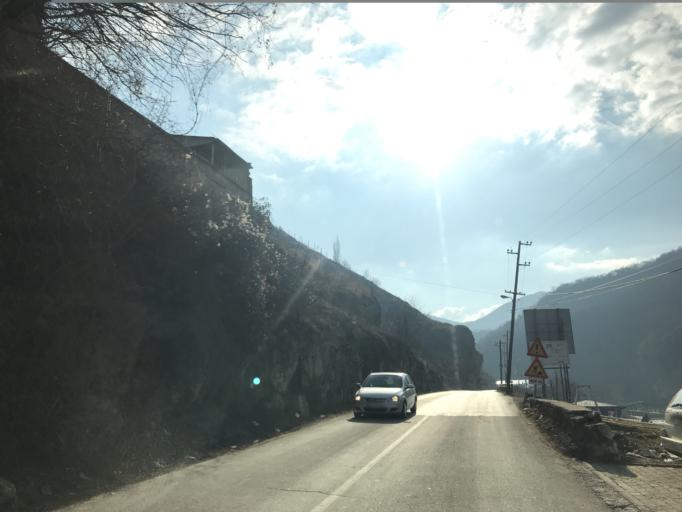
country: XK
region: Prizren
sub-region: Prizren
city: Prizren
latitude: 42.2119
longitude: 20.7468
